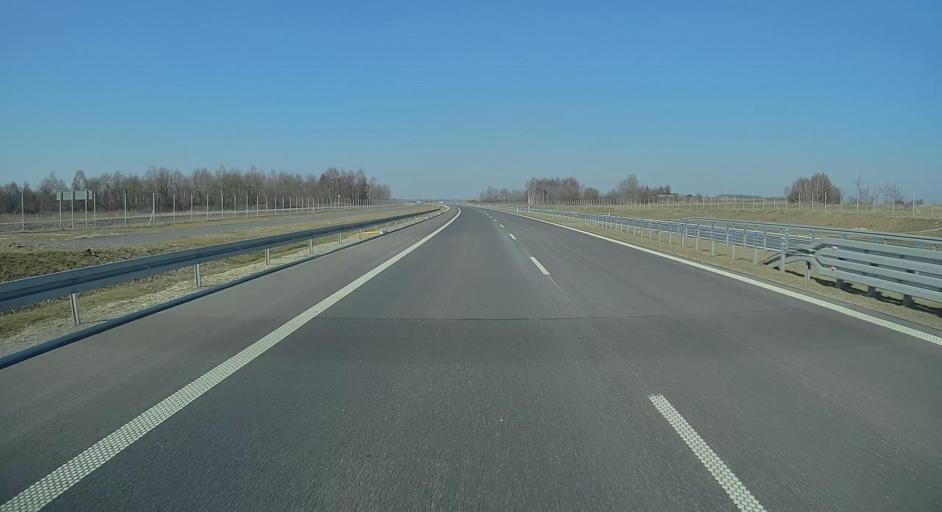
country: PL
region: Lublin Voivodeship
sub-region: Powiat janowski
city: Modliborzyce
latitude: 50.7370
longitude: 22.3378
